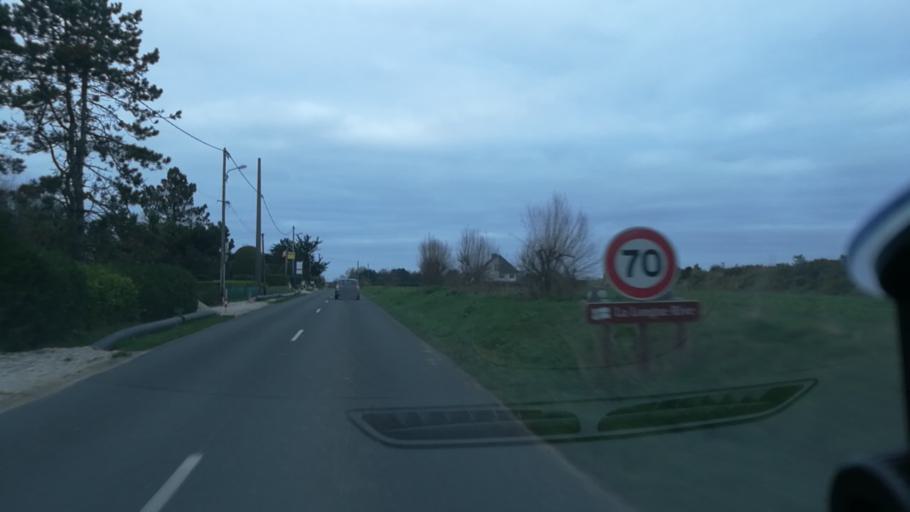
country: FR
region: Lower Normandy
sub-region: Departement de la Manche
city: Reville
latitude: 49.6069
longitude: -1.2581
